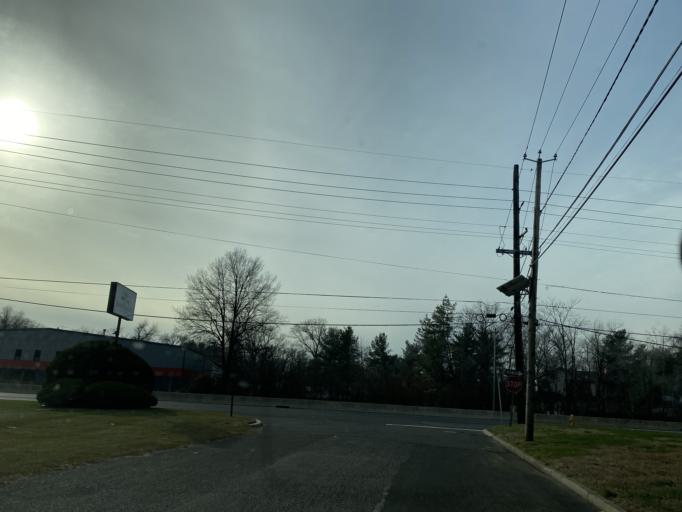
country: US
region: New Jersey
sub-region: Burlington County
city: Maple Shade
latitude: 39.9743
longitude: -75.0089
